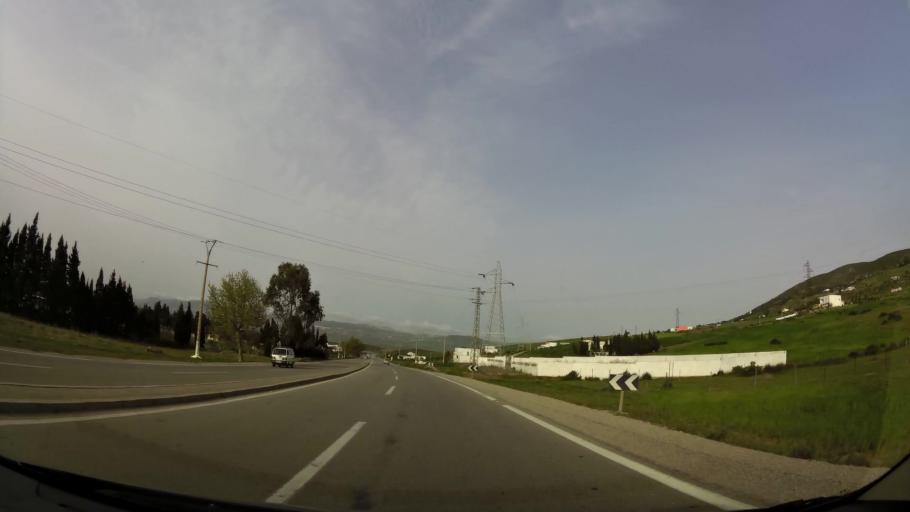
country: MA
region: Tanger-Tetouan
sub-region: Tetouan
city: Saddina
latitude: 35.5543
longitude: -5.5065
